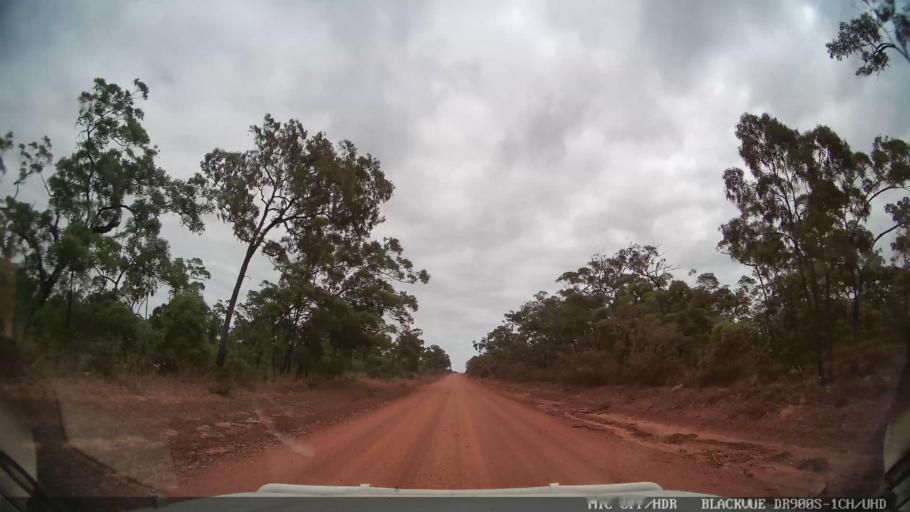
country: AU
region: Queensland
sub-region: Cook
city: Cooktown
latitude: -15.2661
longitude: 144.9483
